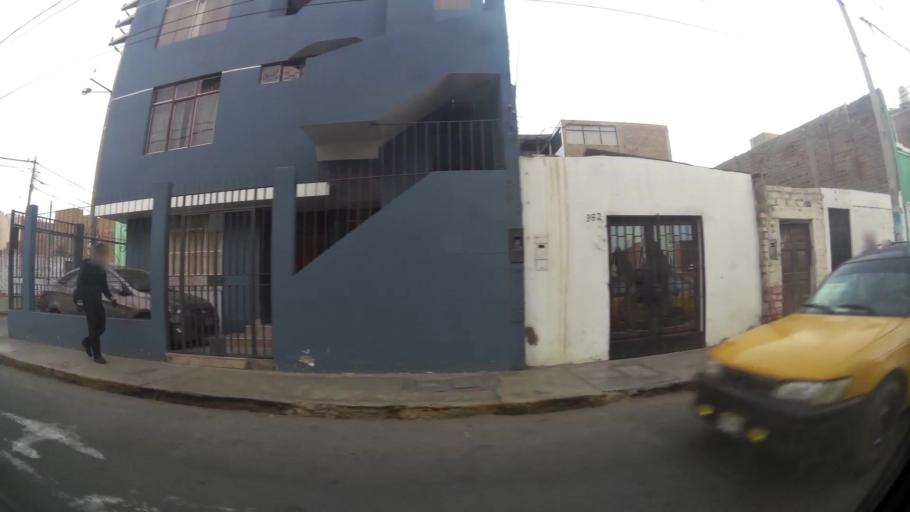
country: PE
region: La Libertad
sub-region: Provincia de Trujillo
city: Trujillo
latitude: -8.1004
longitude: -79.0405
